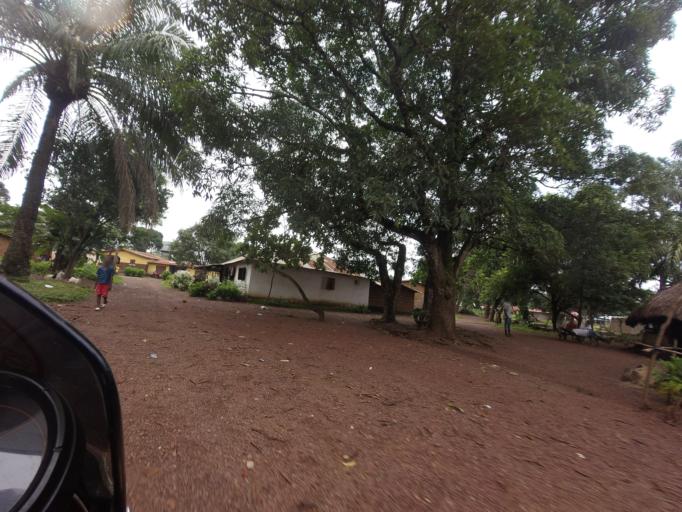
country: SL
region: Northern Province
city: Kambia
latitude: 9.1286
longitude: -12.9095
